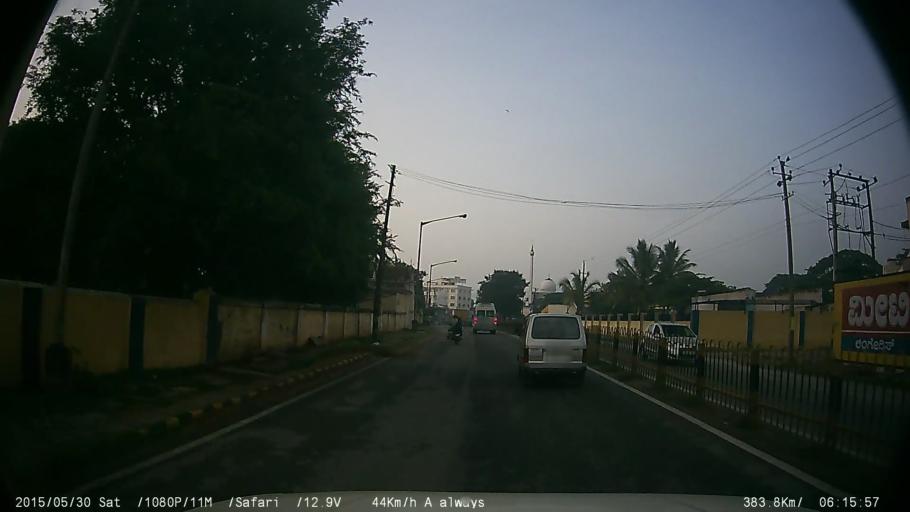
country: IN
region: Karnataka
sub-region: Mysore
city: Mysore
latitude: 12.3213
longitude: 76.6611
